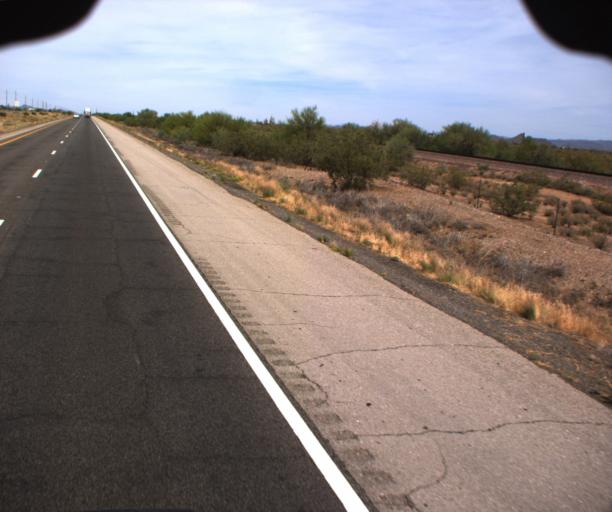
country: US
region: Arizona
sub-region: Maricopa County
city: Wickenburg
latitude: 33.8094
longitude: -112.5688
